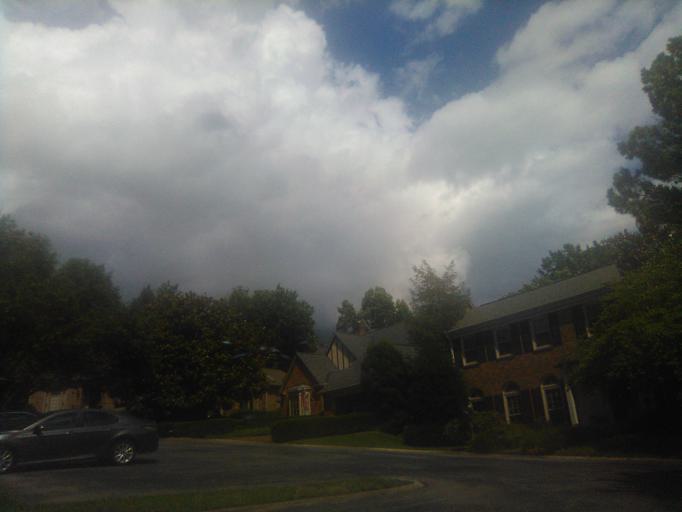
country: US
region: Tennessee
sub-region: Davidson County
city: Belle Meade
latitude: 36.1131
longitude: -86.8314
